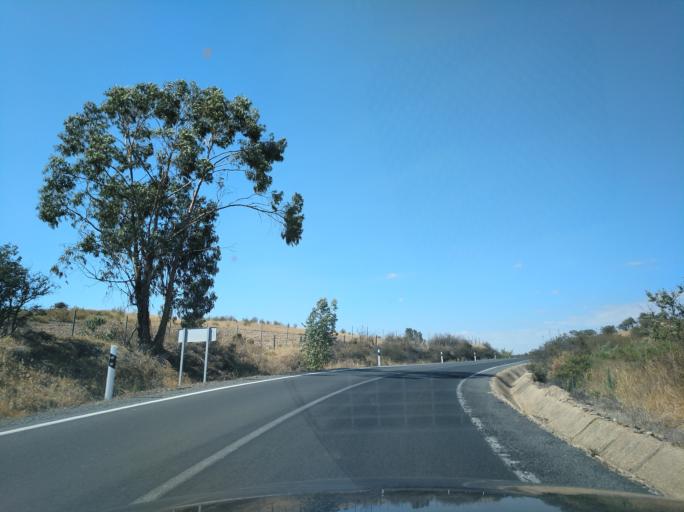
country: ES
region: Andalusia
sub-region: Provincia de Huelva
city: San Bartolome de la Torre
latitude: 37.4792
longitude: -7.1281
